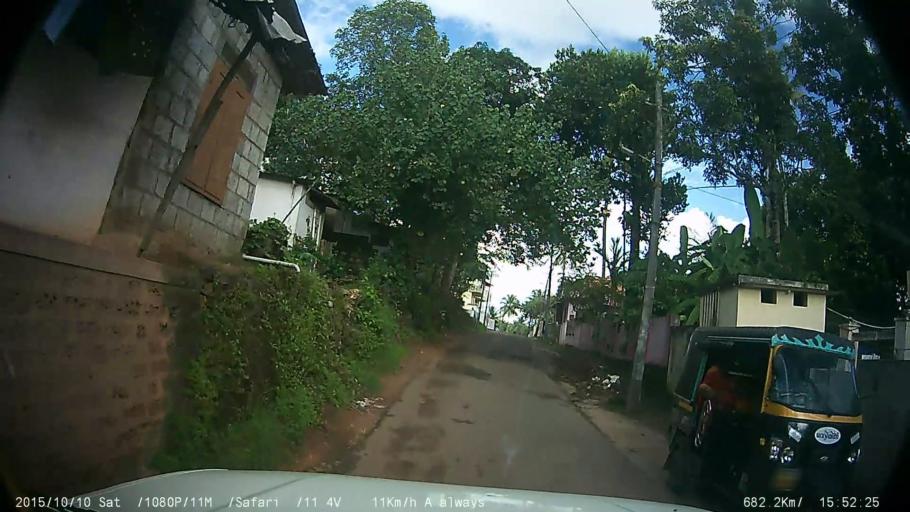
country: IN
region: Kerala
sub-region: Kottayam
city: Changanacheri
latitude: 9.4419
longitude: 76.5546
